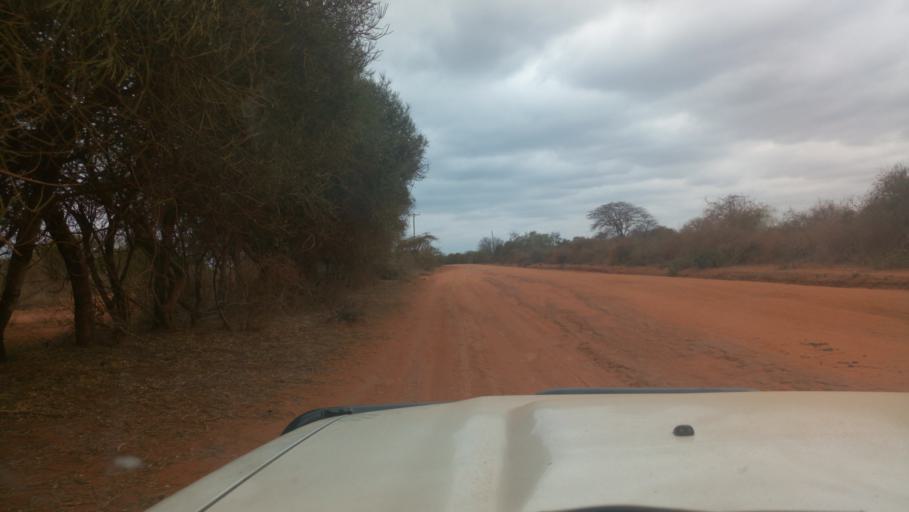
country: KE
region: Makueni
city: Wote
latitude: -1.9063
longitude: 38.0172
